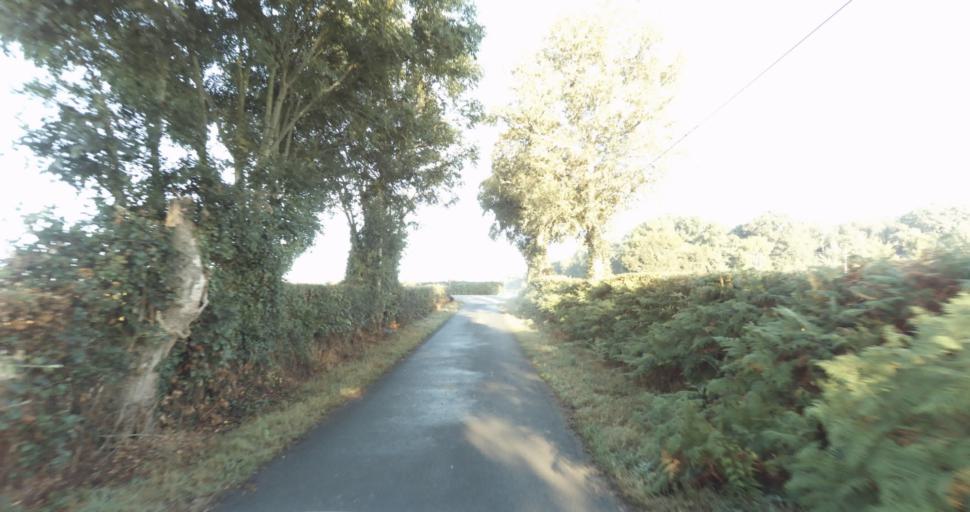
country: FR
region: Lower Normandy
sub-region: Departement de l'Orne
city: Vimoutiers
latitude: 48.9192
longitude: 0.1530
